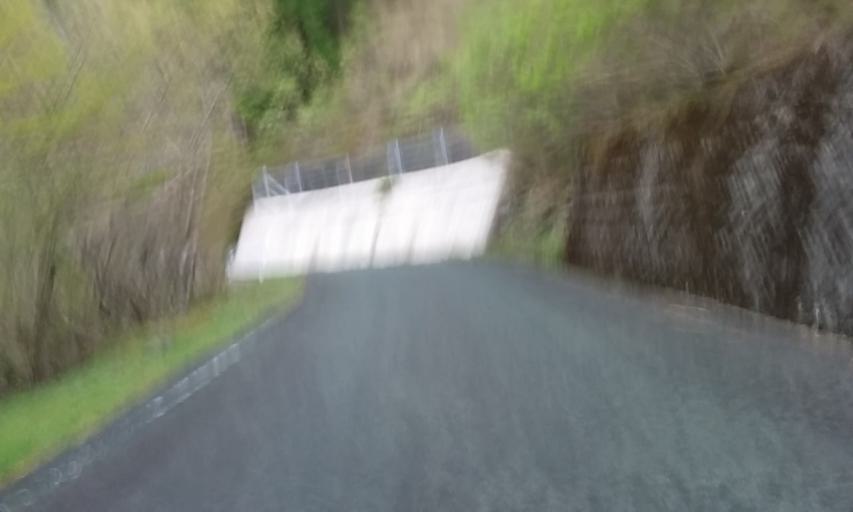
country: JP
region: Ehime
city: Saijo
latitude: 33.7868
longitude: 133.2808
